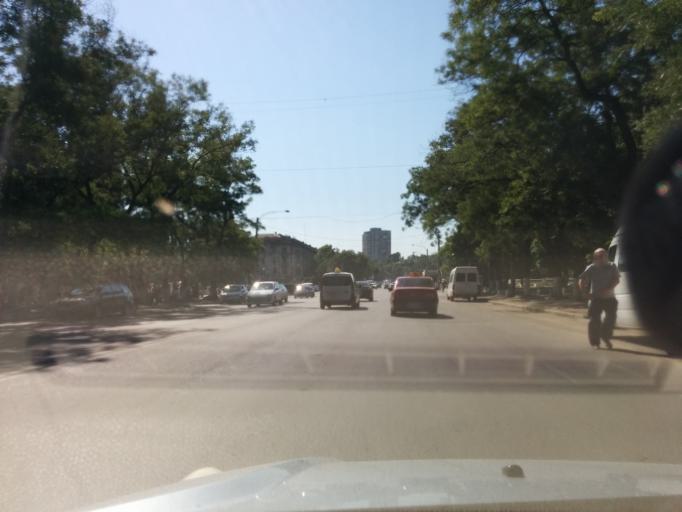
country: MD
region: Chisinau
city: Chisinau
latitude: 47.0122
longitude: 28.8566
